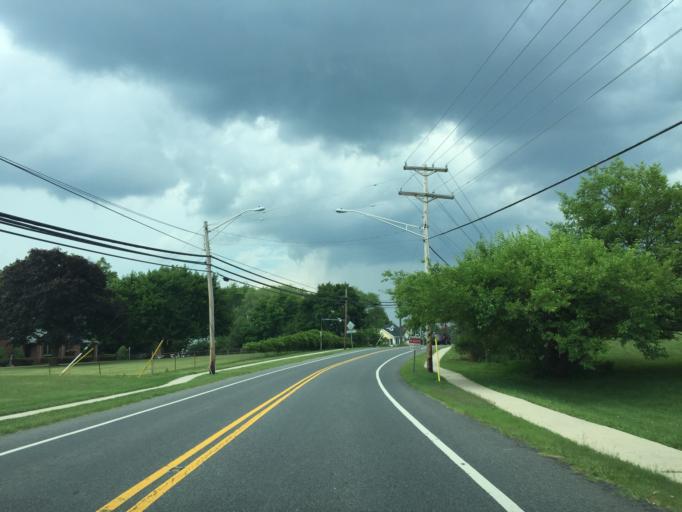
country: US
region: Maryland
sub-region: Montgomery County
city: Burtonsville
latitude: 39.0986
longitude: -76.9442
